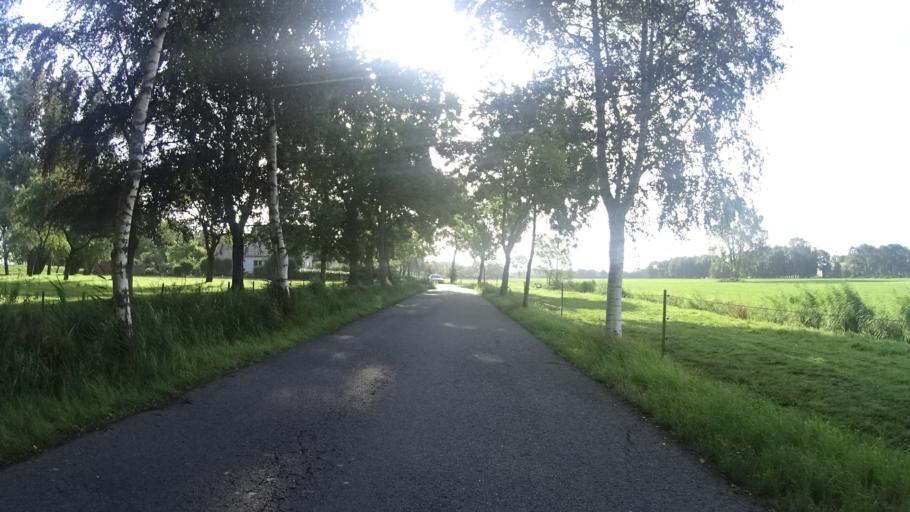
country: DE
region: Lower Saxony
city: Nordenham
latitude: 53.4948
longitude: 8.4459
